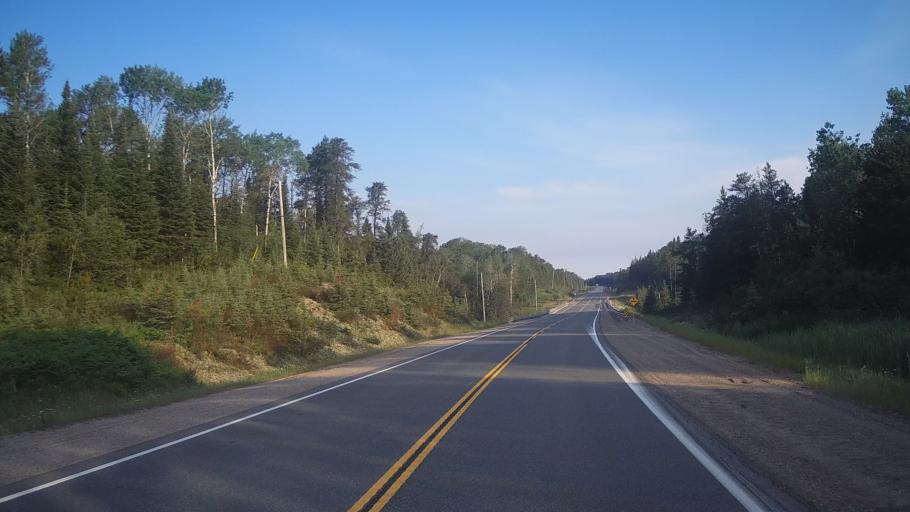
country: CA
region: Ontario
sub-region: Rainy River District
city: Atikokan
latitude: 49.3517
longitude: -91.5211
